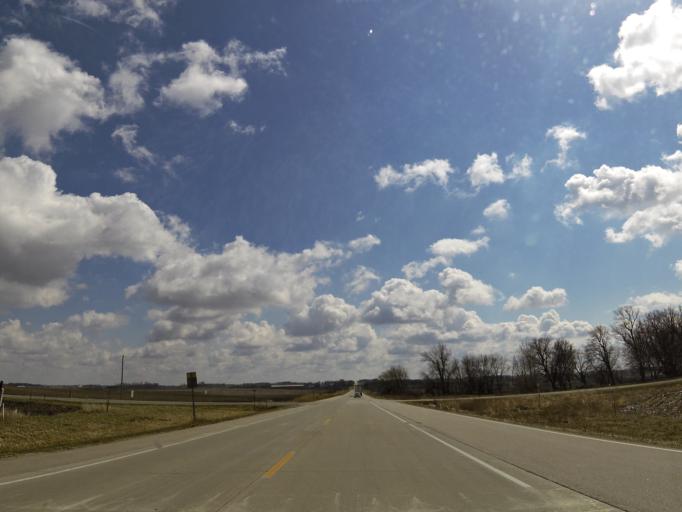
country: US
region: Minnesota
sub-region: Dodge County
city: Dodge Center
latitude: 44.0890
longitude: -92.8995
